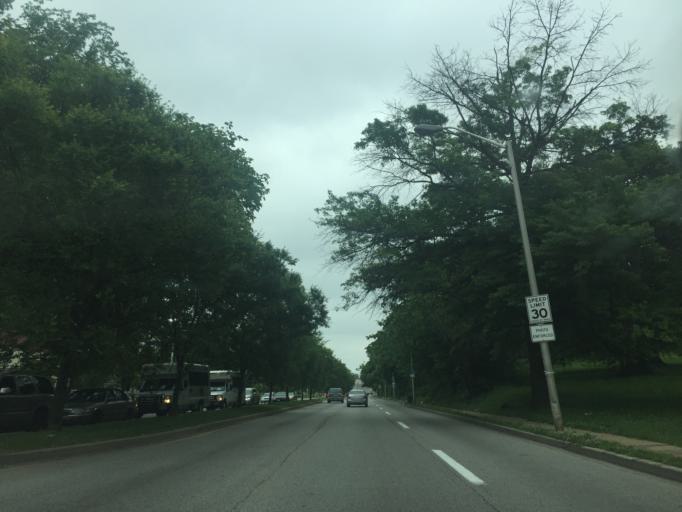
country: US
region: Maryland
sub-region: Baltimore County
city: Lochearn
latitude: 39.3238
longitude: -76.6706
